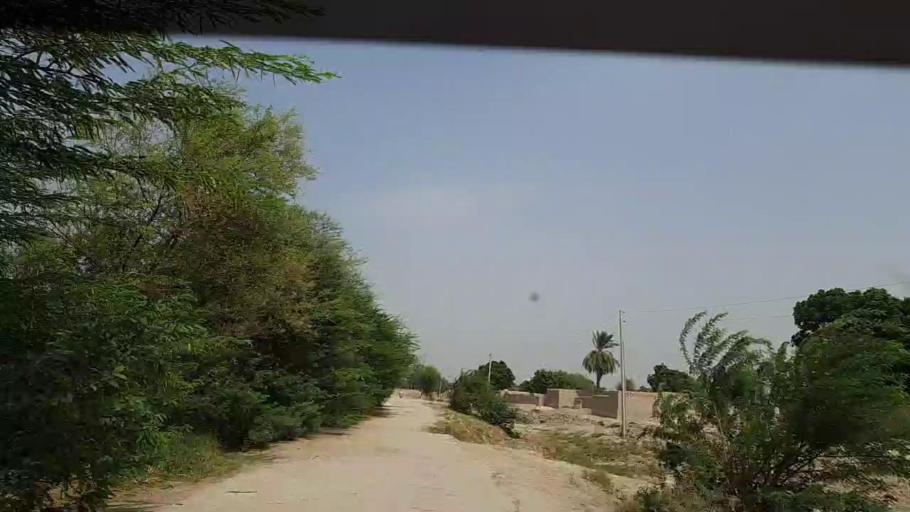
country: PK
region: Sindh
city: Khairpur Nathan Shah
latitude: 27.0810
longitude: 67.6699
